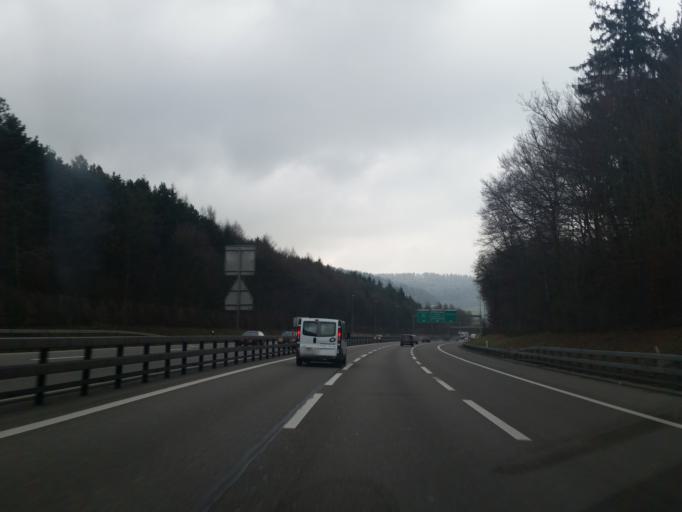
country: CH
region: Zurich
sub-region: Bezirk Dietikon
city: Dietikon / Schoenenwerd
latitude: 47.4047
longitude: 8.4219
